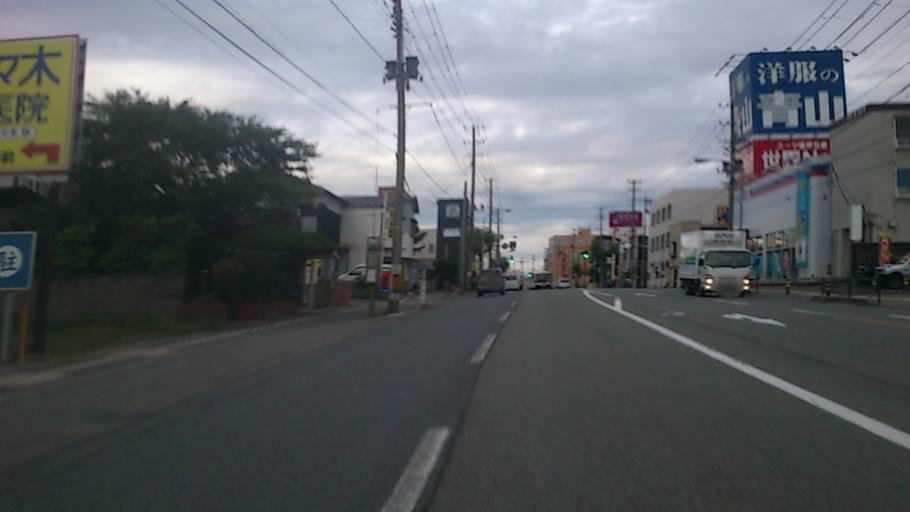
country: JP
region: Akita
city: Akita Shi
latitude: 39.7494
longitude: 140.0705
